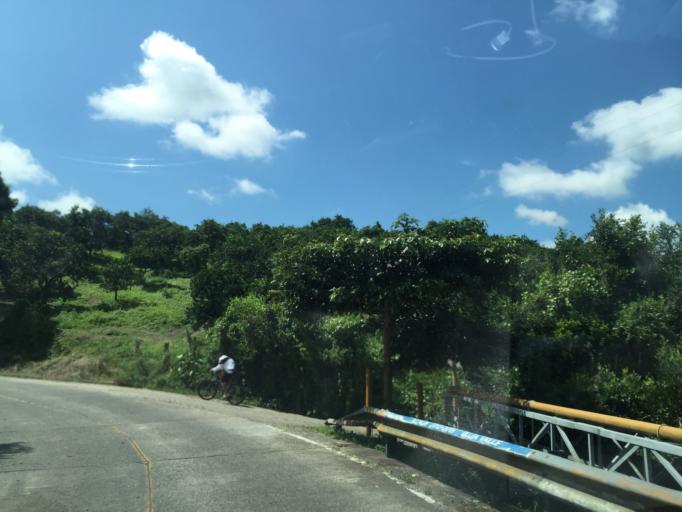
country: CO
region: Valle del Cauca
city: Ulloa
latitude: 4.7006
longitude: -75.7655
